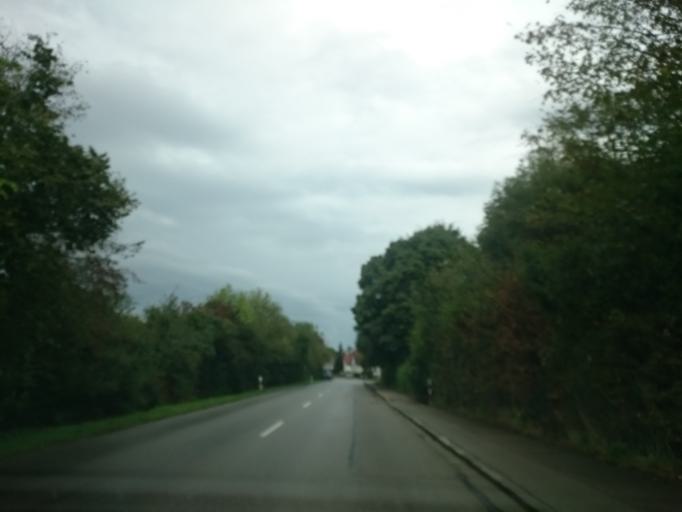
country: DE
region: Bavaria
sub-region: Swabia
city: Kleinaitingen
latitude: 48.2150
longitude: 10.8384
